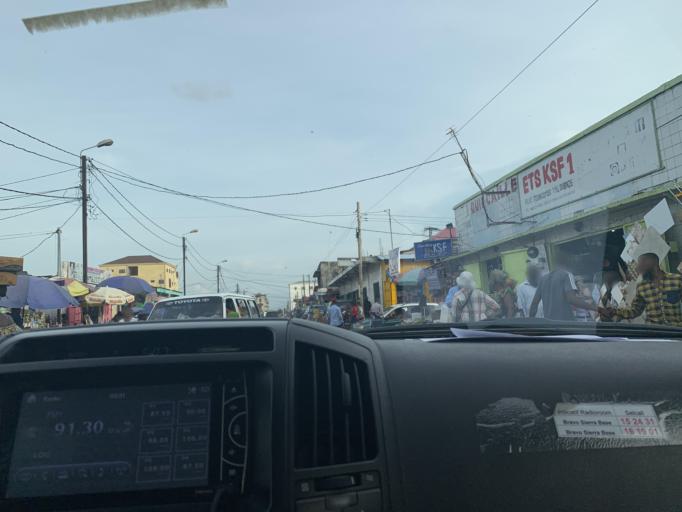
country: CG
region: Brazzaville
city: Brazzaville
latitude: -4.2471
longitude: 15.2827
